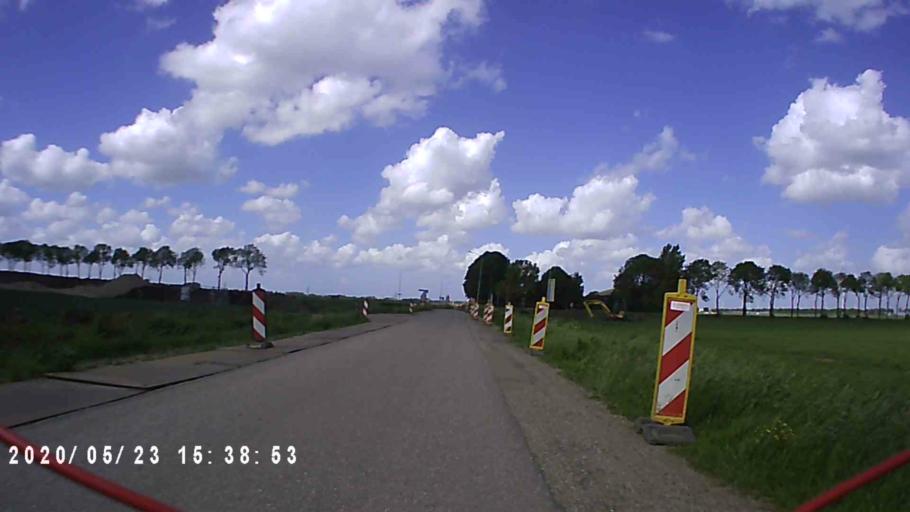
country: NL
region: Groningen
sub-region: Gemeente Delfzijl
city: Delfzijl
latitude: 53.2794
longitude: 6.9407
